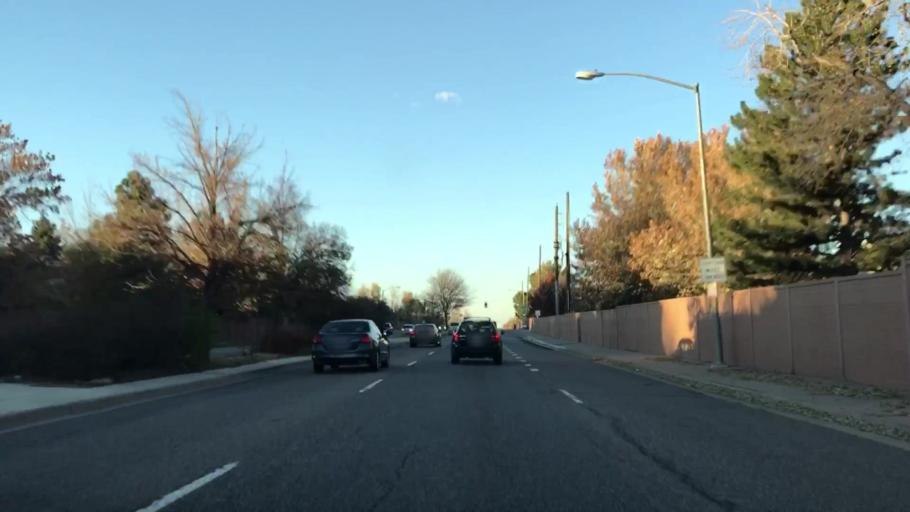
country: US
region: Colorado
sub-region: Arapahoe County
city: Castlewood
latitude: 39.6414
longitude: -104.8850
